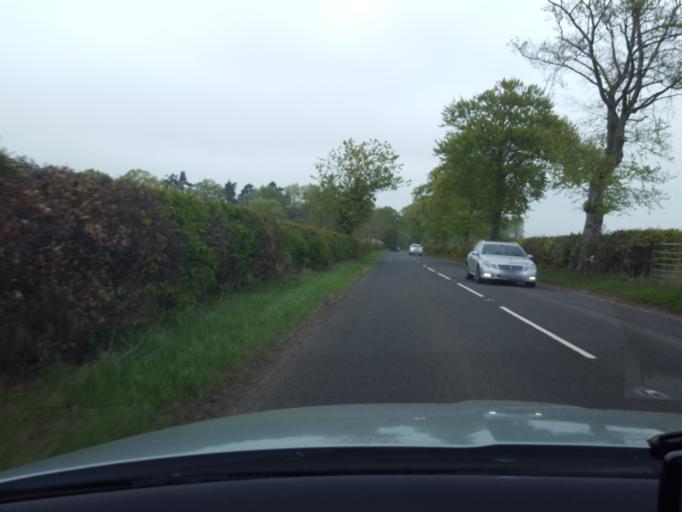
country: GB
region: Scotland
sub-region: Angus
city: Brechin
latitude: 56.7655
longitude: -2.6441
